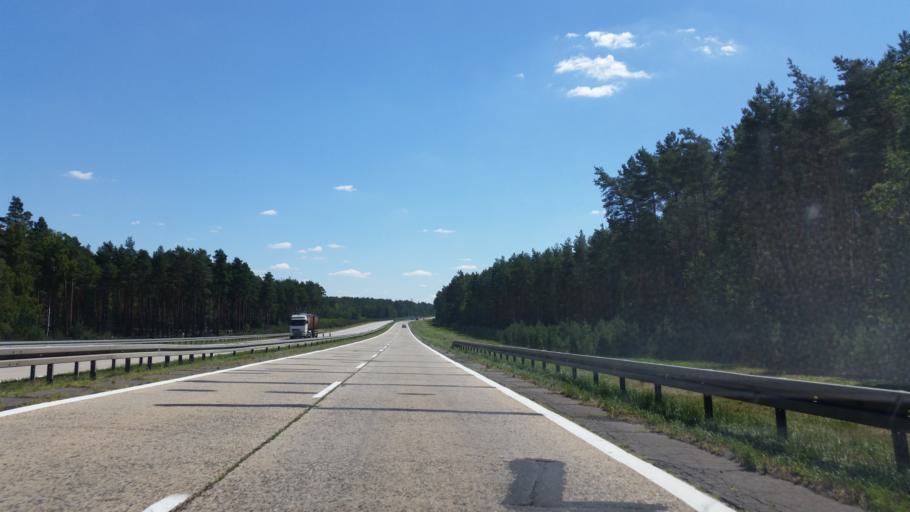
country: PL
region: Lower Silesian Voivodeship
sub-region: Powiat boleslawiecki
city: Boleslawiec
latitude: 51.4028
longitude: 15.5146
